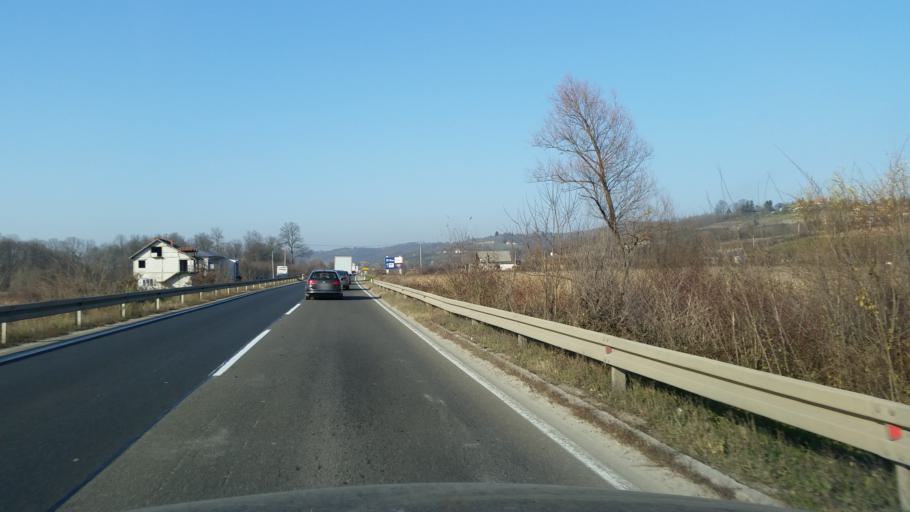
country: RS
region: Central Serbia
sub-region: Belgrade
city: Lazarevac
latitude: 44.3240
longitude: 20.2238
